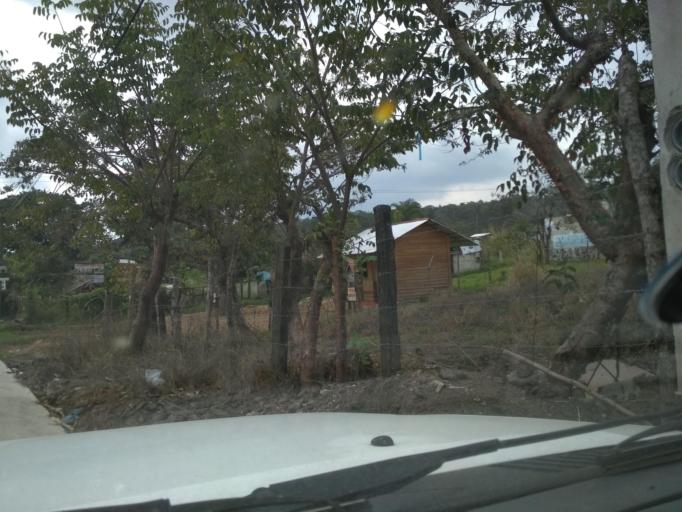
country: MX
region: Veracruz
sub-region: Coatepec
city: Bella Esperanza
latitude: 19.4553
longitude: -96.8624
